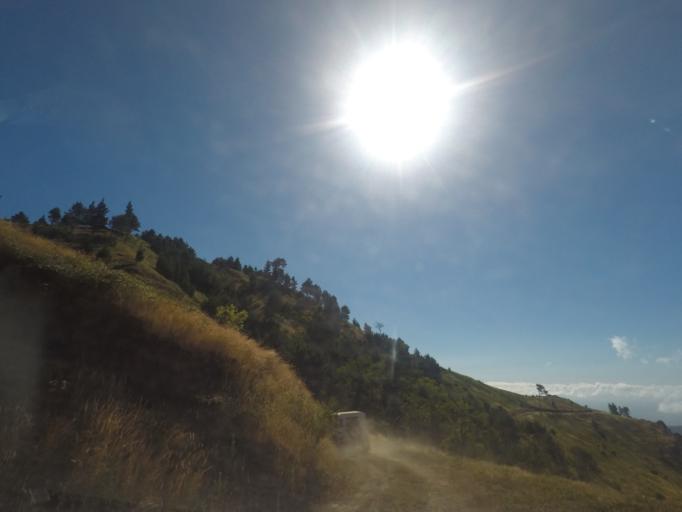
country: PT
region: Madeira
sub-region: Funchal
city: Nossa Senhora do Monte
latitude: 32.7047
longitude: -16.9097
